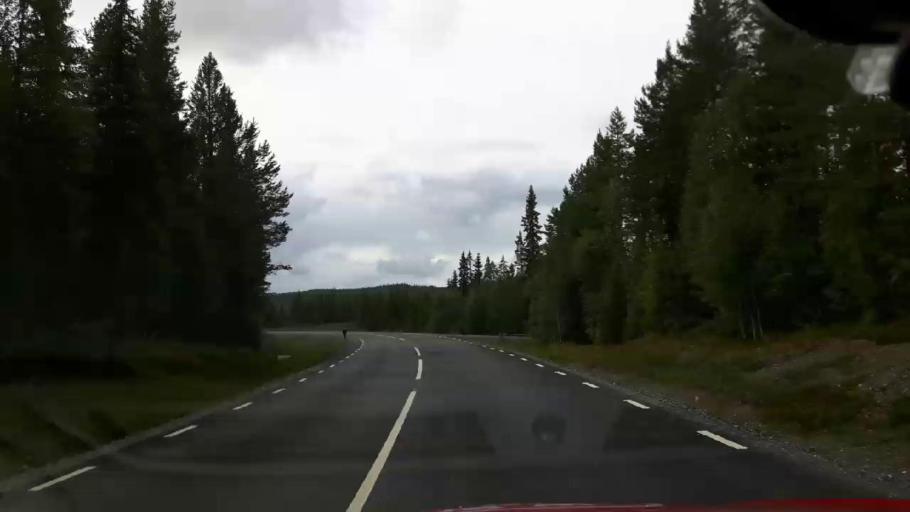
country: NO
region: Nord-Trondelag
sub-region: Lierne
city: Sandvika
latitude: 64.6280
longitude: 14.1253
